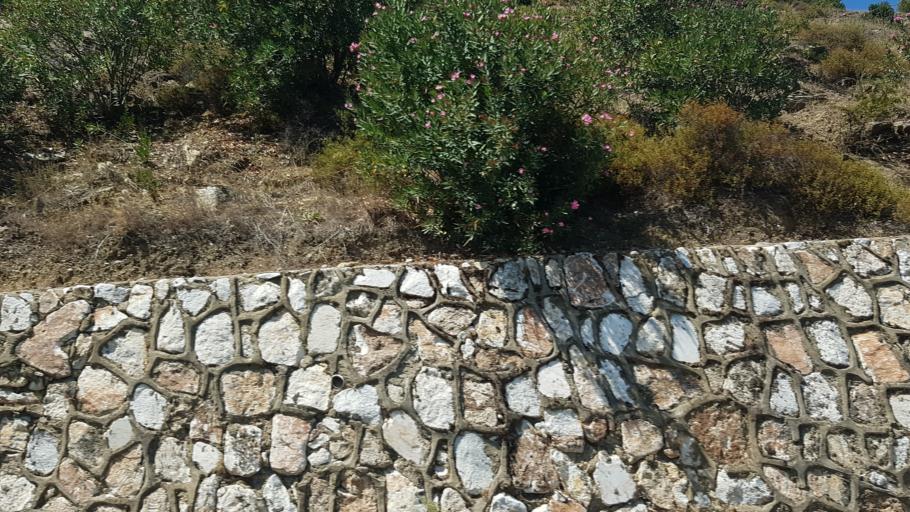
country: TR
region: Aydin
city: Akcaova
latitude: 37.5073
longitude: 28.1021
